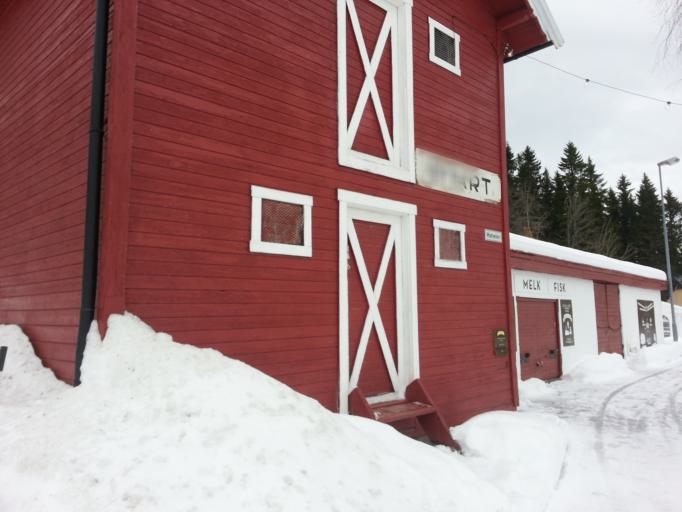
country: NO
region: Sor-Trondelag
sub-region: Trondheim
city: Trondheim
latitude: 63.4028
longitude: 10.3103
